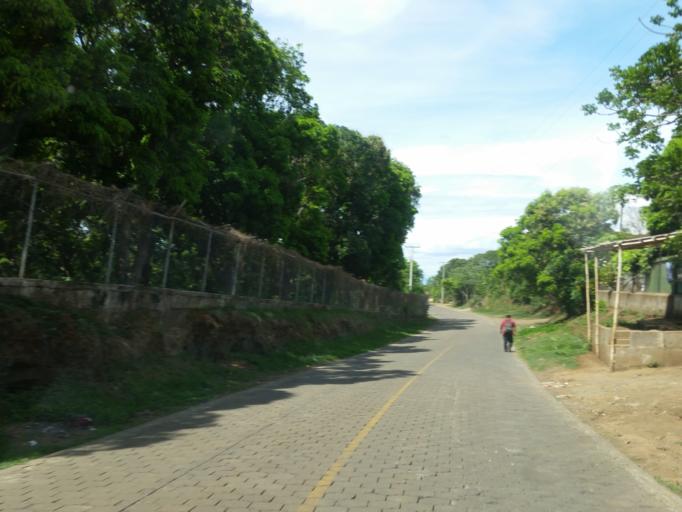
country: NI
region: Masaya
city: Masaya
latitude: 11.9698
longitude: -86.0294
